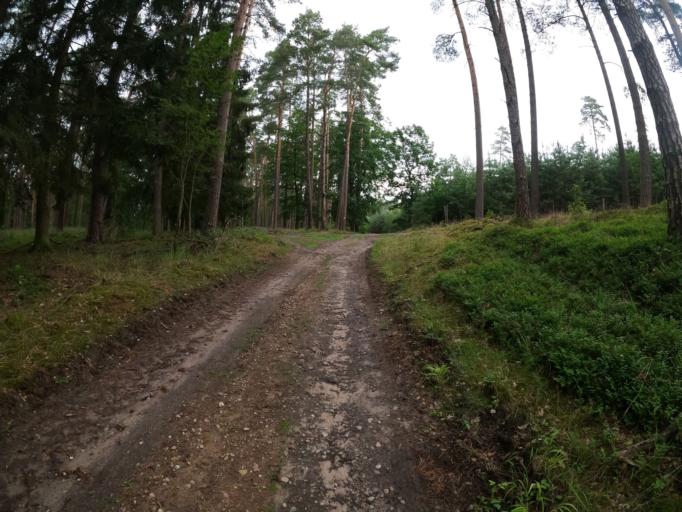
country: DE
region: Brandenburg
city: Althuttendorf
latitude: 53.0372
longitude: 13.8865
